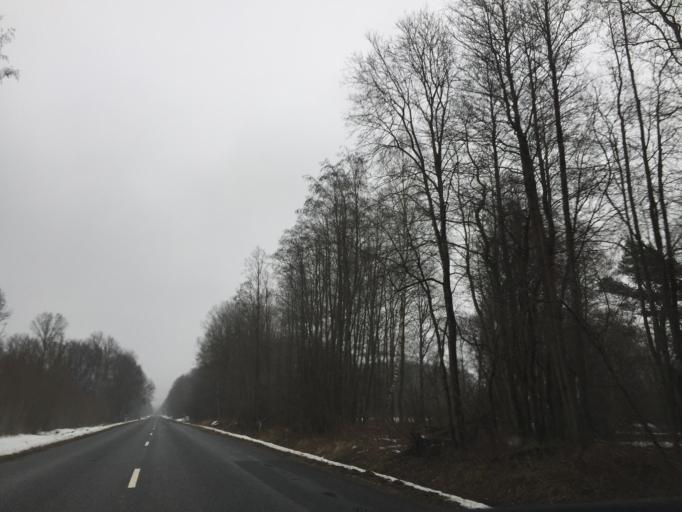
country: EE
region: Saare
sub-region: Kuressaare linn
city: Kuressaare
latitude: 58.3467
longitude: 22.7941
